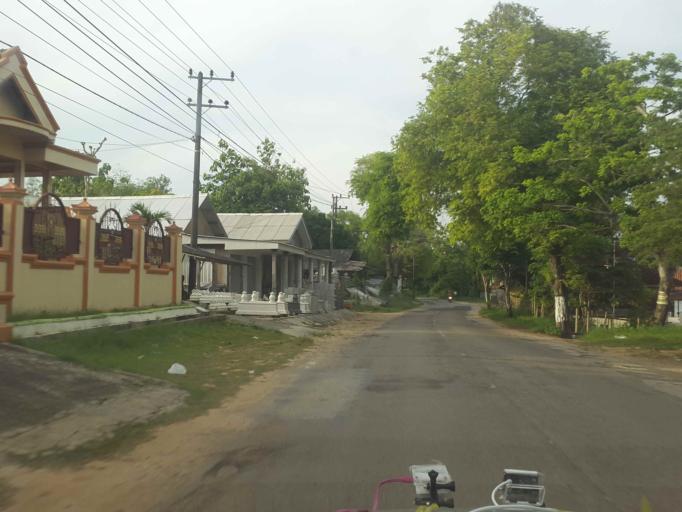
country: ID
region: East Java
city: Senmasen
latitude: -6.9939
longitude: 113.8663
